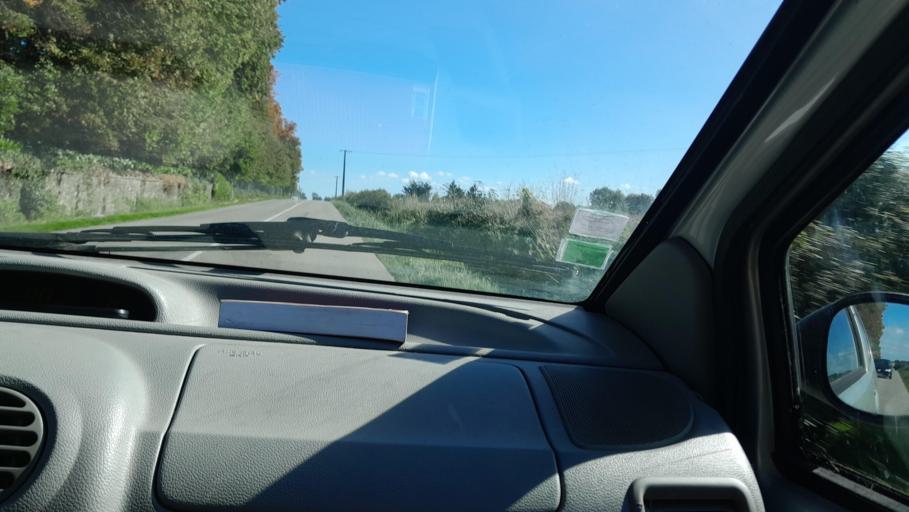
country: FR
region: Pays de la Loire
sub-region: Departement de la Mayenne
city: Quelaines-Saint-Gault
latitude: 47.9359
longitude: -0.8563
